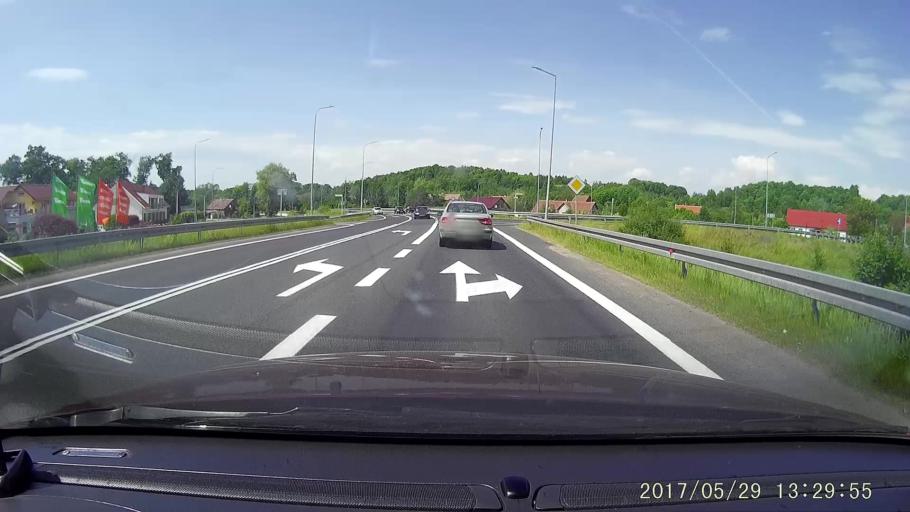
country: PL
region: Lower Silesian Voivodeship
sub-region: Powiat lubanski
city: Olszyna
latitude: 51.0736
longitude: 15.3608
